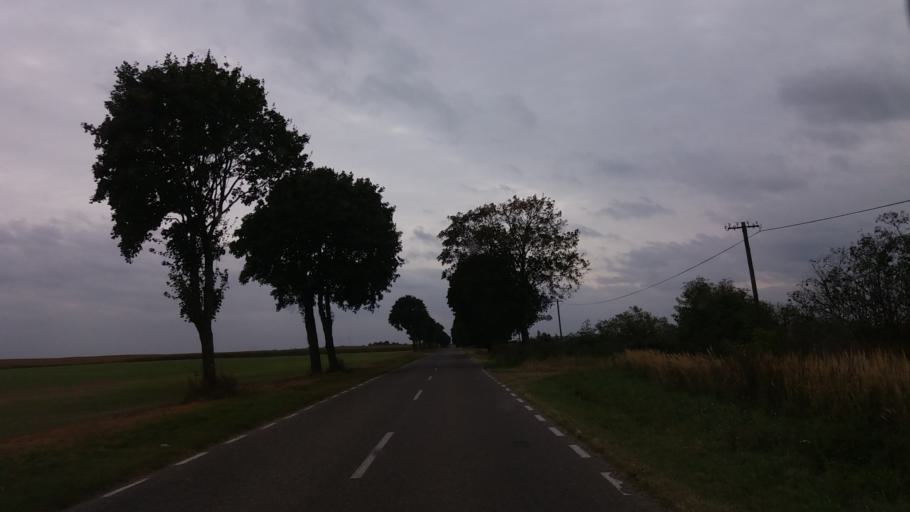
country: PL
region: Lubusz
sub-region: Powiat strzelecko-drezdenecki
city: Strzelce Krajenskie
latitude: 52.9520
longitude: 15.5705
